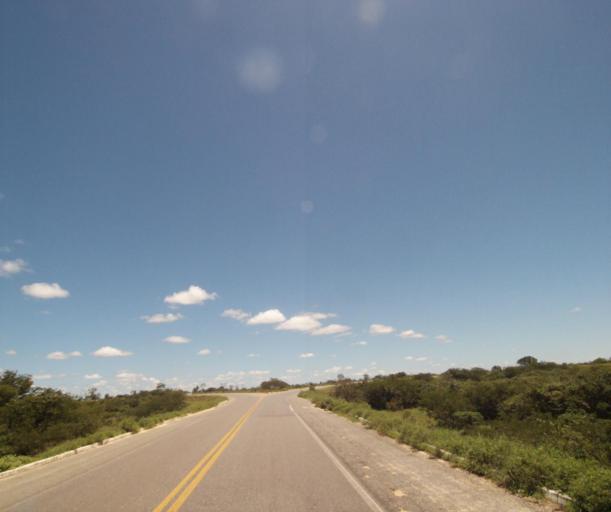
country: BR
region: Bahia
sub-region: Carinhanha
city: Carinhanha
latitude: -14.2889
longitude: -43.7847
